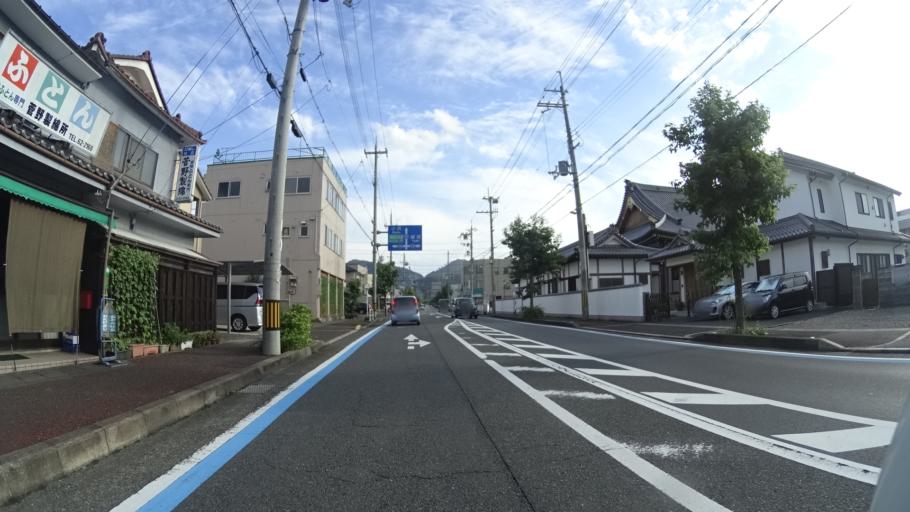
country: JP
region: Kyoto
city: Maizuru
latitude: 35.4624
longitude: 135.3975
